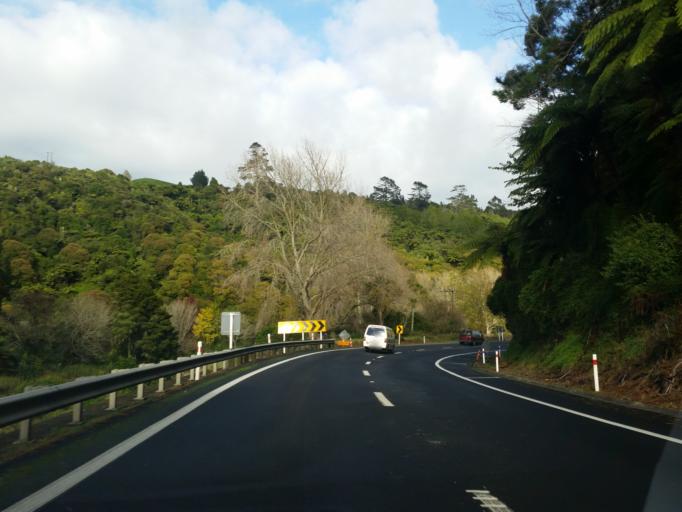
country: NZ
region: Waikato
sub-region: Hauraki District
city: Waihi
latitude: -37.4187
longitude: 175.7531
